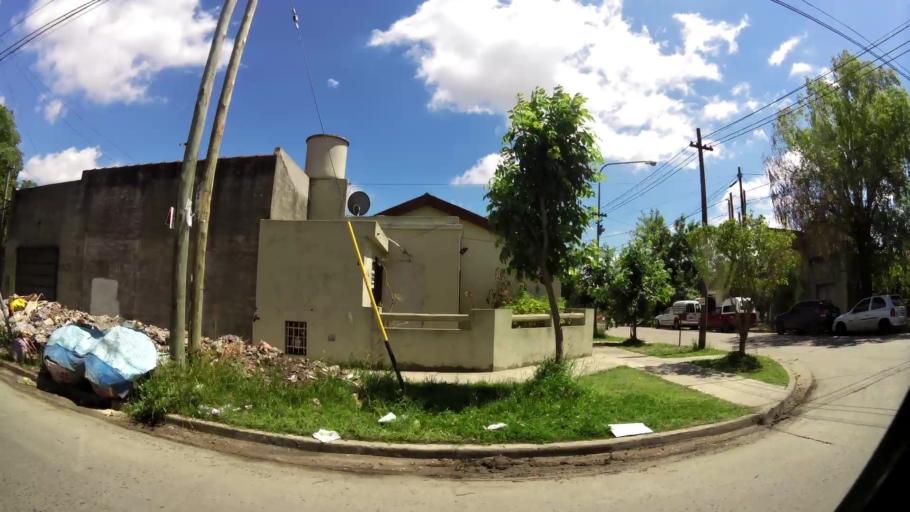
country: AR
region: Buenos Aires
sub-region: Partido de Lanus
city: Lanus
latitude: -34.7010
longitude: -58.4202
